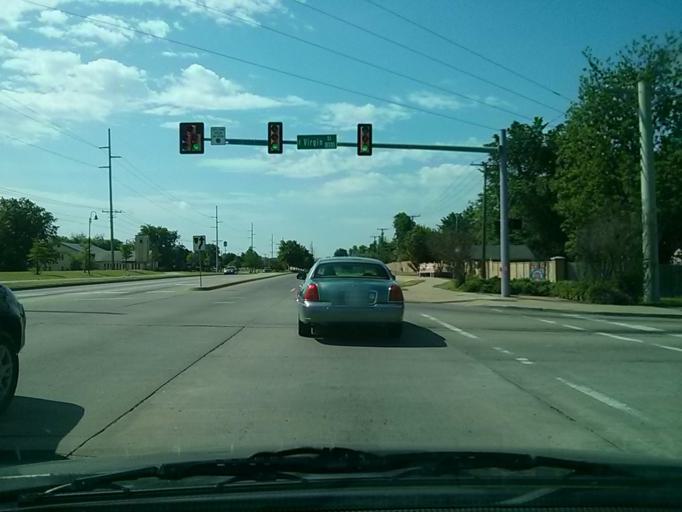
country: US
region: Oklahoma
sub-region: Tulsa County
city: Tulsa
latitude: 36.1843
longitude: -95.9760
